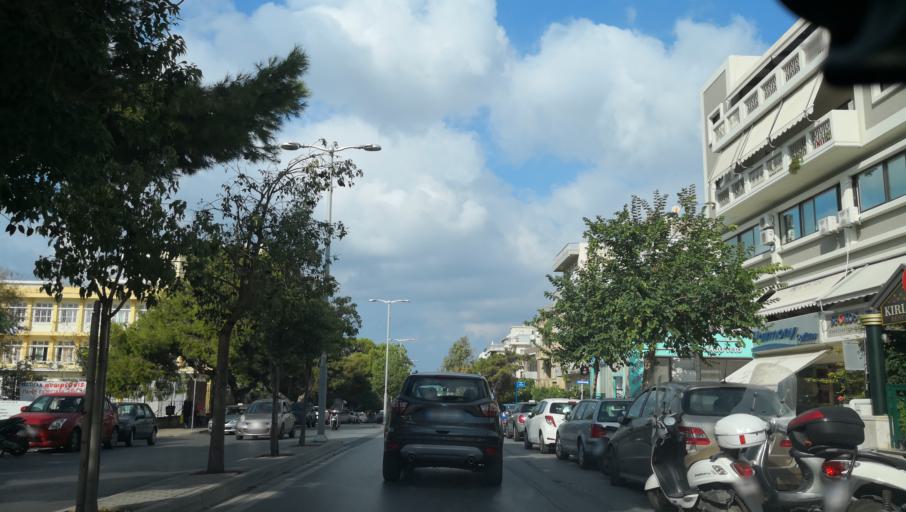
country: GR
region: Crete
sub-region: Nomos Irakleiou
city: Irakleion
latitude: 35.3331
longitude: 25.1385
